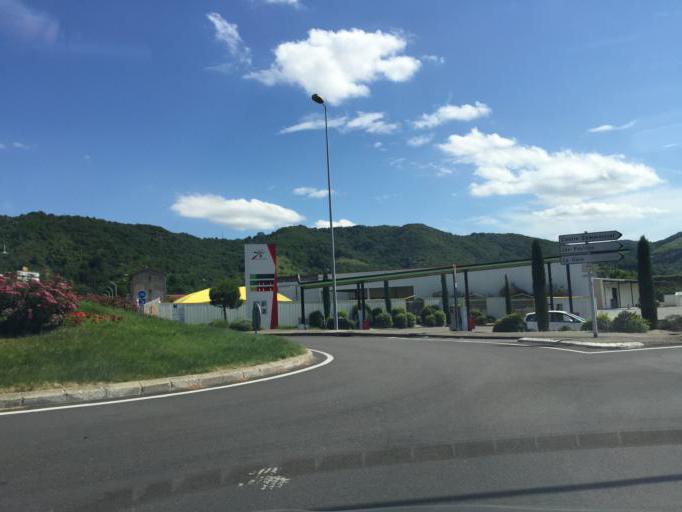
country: FR
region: Rhone-Alpes
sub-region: Departement de l'Ardeche
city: Saint-Jean-de-Muzols
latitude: 45.0766
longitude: 4.8155
